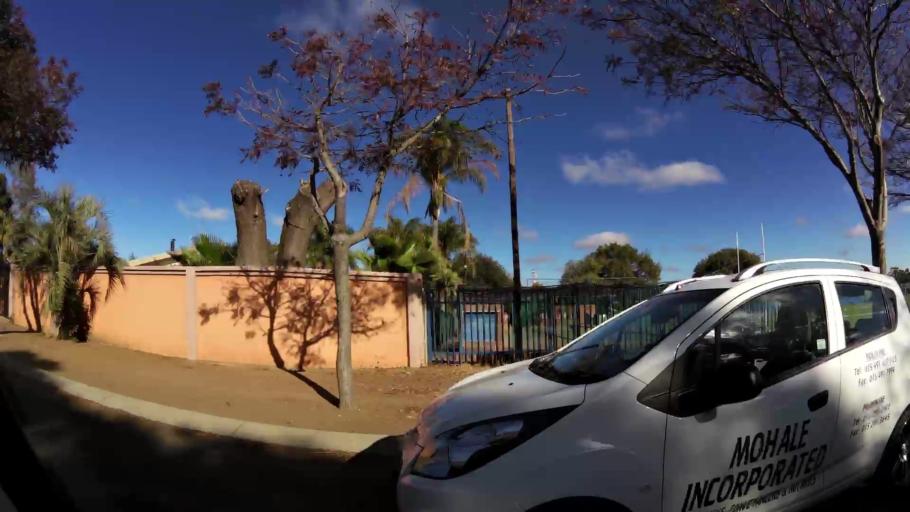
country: ZA
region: Limpopo
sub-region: Capricorn District Municipality
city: Polokwane
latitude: -23.9115
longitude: 29.4604
